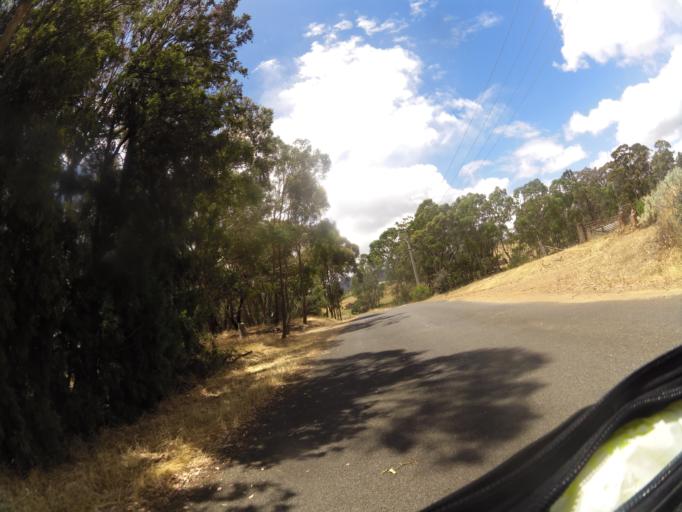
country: AU
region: Victoria
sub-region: Mount Alexander
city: Castlemaine
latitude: -37.0207
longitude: 144.2502
